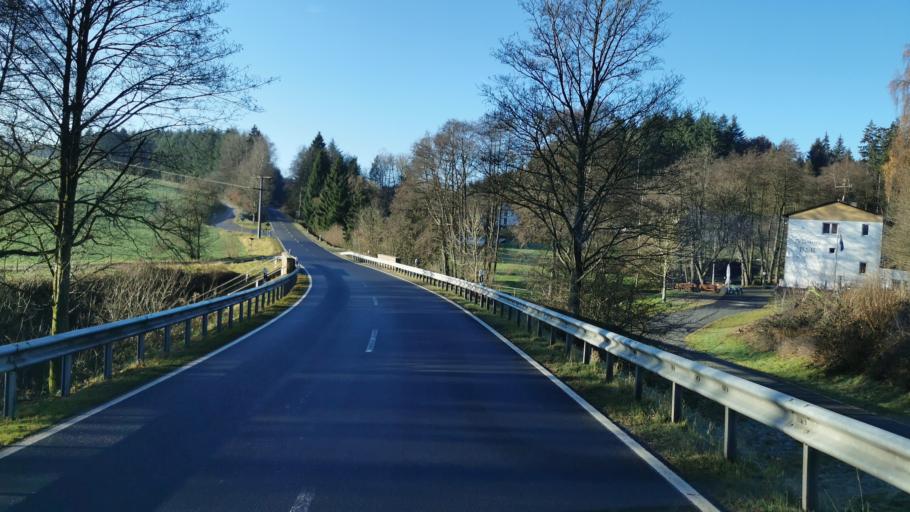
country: DE
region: Rheinland-Pfalz
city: Meisburg
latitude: 50.1076
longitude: 6.6783
